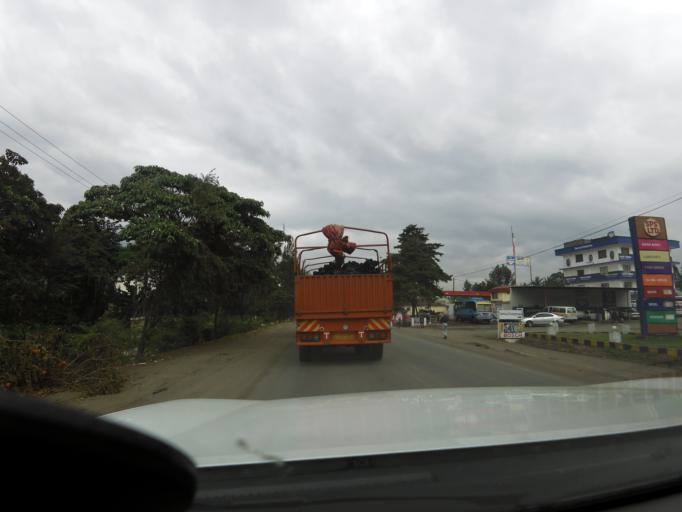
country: TZ
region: Arusha
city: Arusha
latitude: -3.3623
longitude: 36.6816
